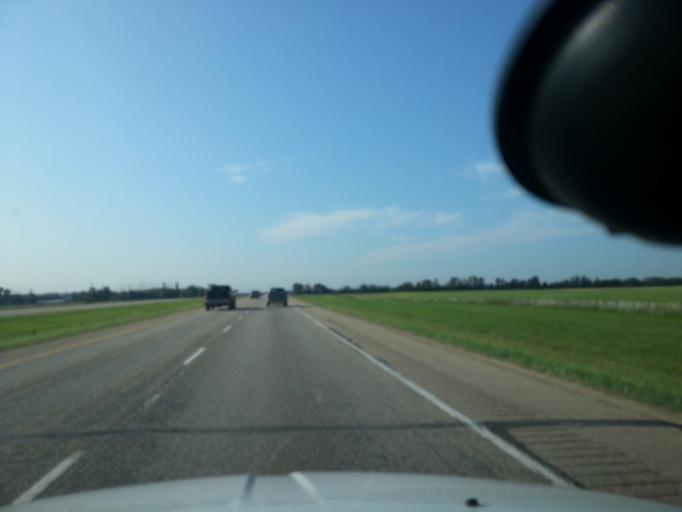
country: CA
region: Alberta
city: Ponoka
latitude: 52.8782
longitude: -113.6442
